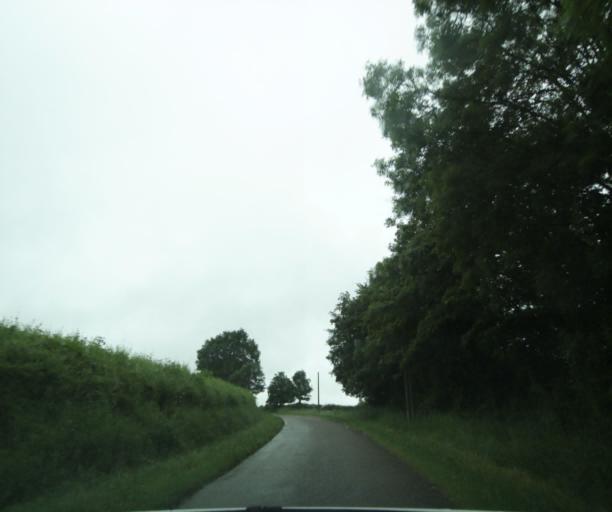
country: FR
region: Bourgogne
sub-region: Departement de Saone-et-Loire
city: Paray-le-Monial
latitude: 46.4753
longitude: 4.1821
